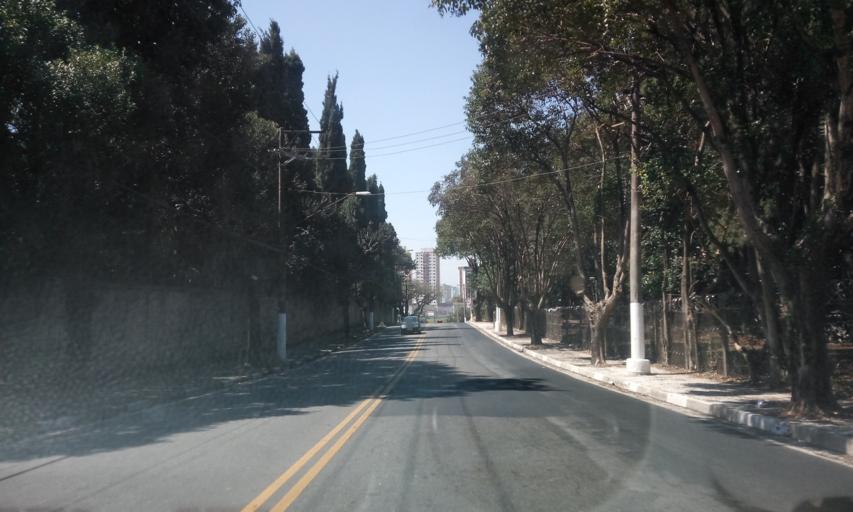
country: BR
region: Sao Paulo
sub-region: Sao Bernardo Do Campo
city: Sao Bernardo do Campo
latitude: -23.6992
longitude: -46.5663
